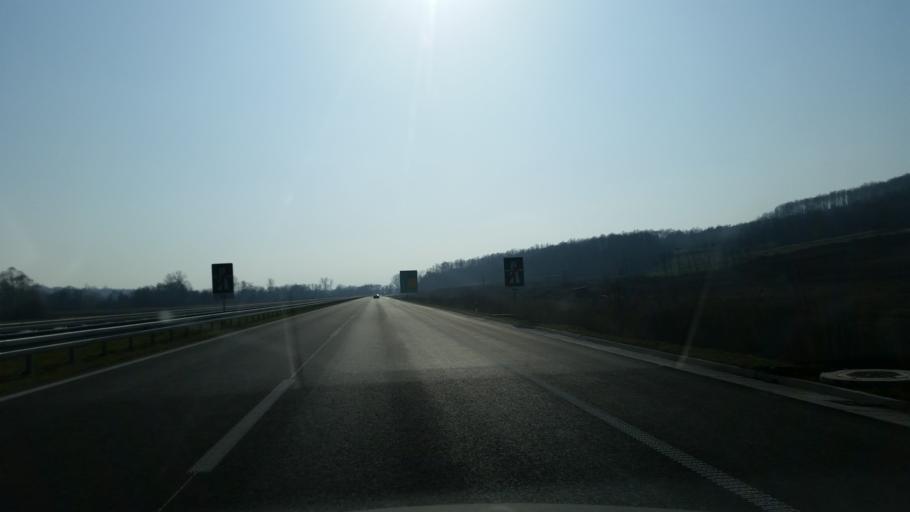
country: RS
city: Prislonica
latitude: 43.9362
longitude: 20.4008
